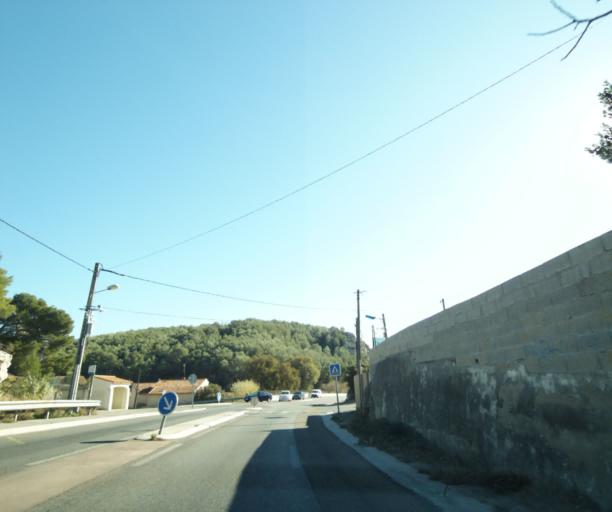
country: FR
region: Provence-Alpes-Cote d'Azur
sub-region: Departement des Bouches-du-Rhone
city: Le Rove
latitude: 43.3676
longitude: 5.2624
